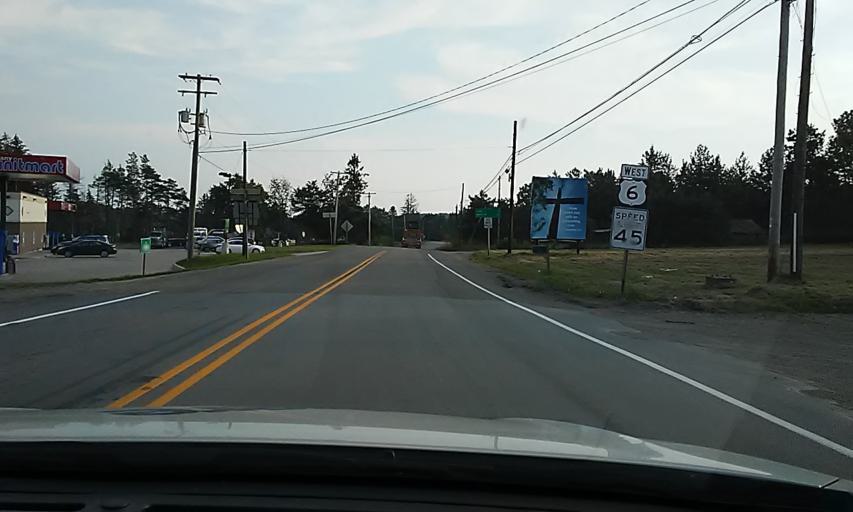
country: US
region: Pennsylvania
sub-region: McKean County
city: Kane
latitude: 41.7078
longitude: -78.6944
